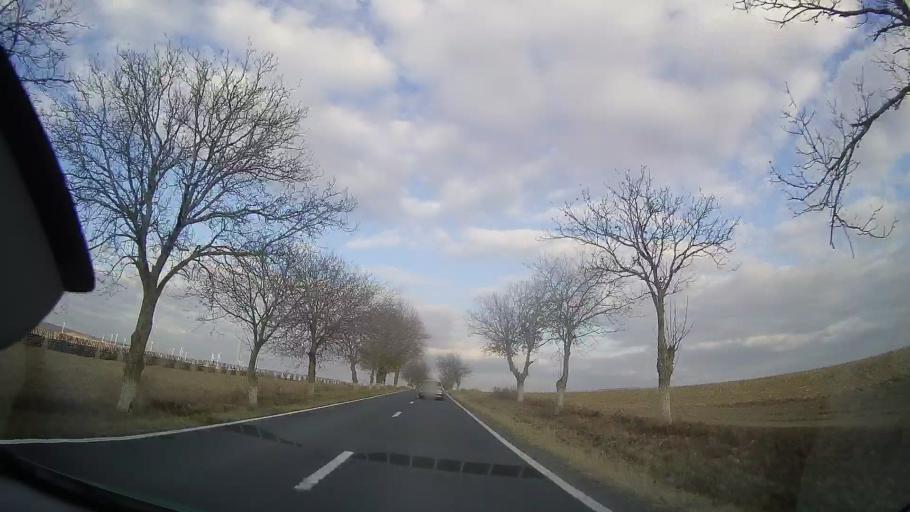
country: RO
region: Tulcea
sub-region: Comuna Topolog
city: Topolog
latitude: 44.8538
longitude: 28.3312
